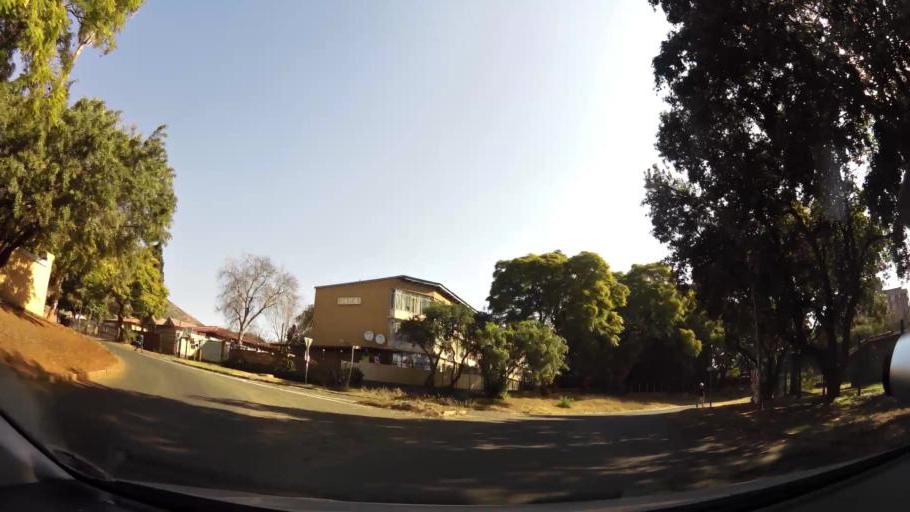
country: ZA
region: Gauteng
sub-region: City of Tshwane Metropolitan Municipality
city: Pretoria
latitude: -25.6814
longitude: 28.1721
